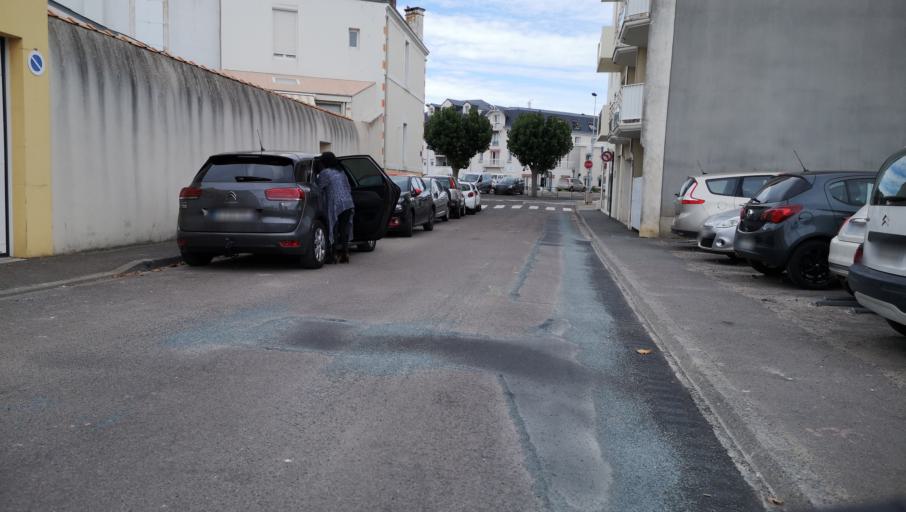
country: FR
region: Pays de la Loire
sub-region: Departement de la Vendee
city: Les Sables-d'Olonne
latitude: 46.4973
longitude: -1.7795
